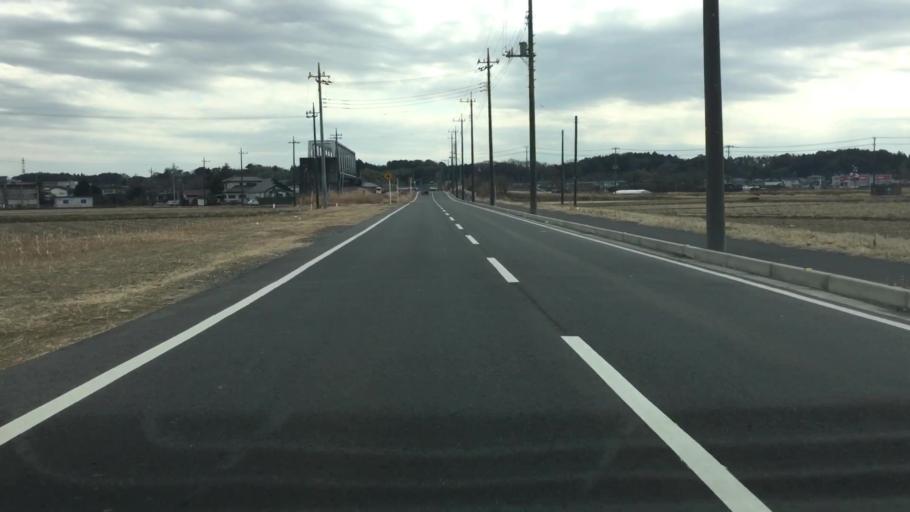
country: JP
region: Ibaraki
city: Ryugasaki
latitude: 35.8404
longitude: 140.1362
